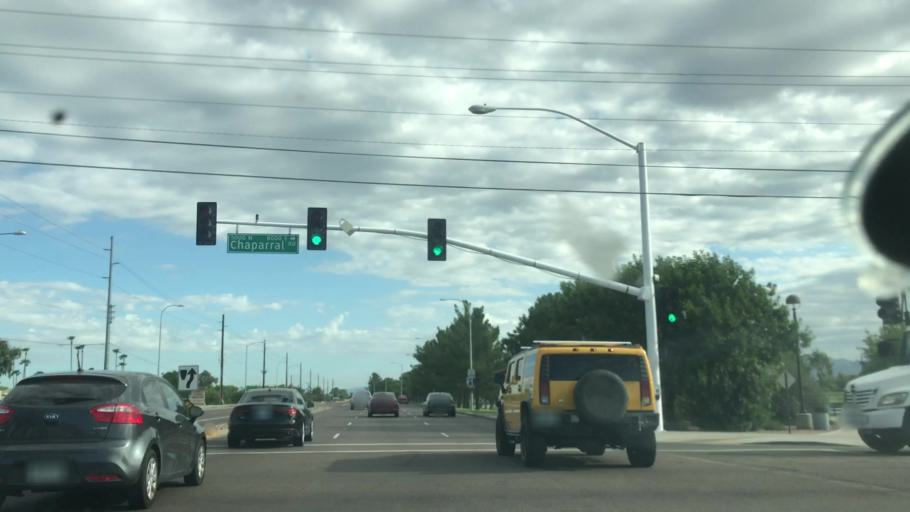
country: US
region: Arizona
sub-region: Maricopa County
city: Scottsdale
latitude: 33.5094
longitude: -111.9086
